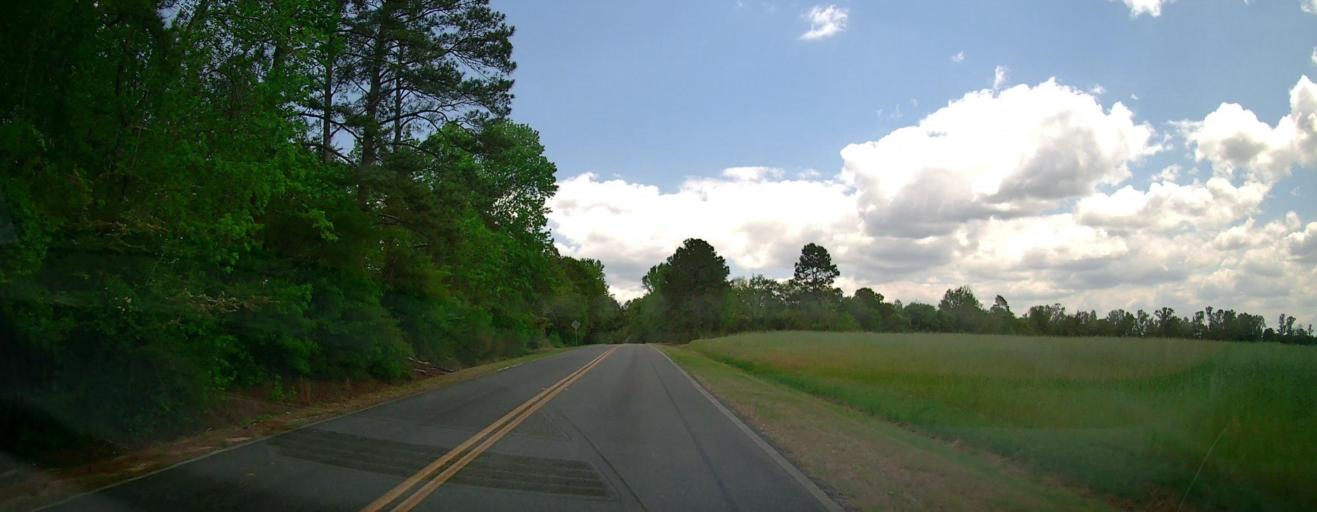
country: US
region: Georgia
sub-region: Treutlen County
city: Soperton
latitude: 32.5195
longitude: -82.6656
